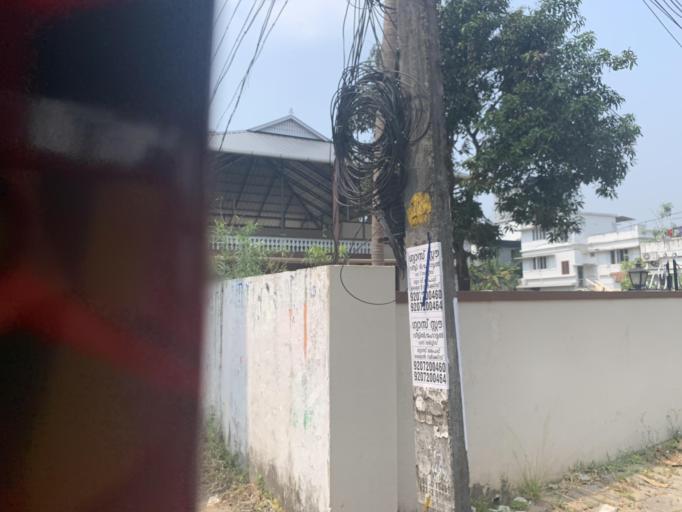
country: IN
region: Kerala
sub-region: Ernakulam
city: Cochin
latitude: 9.9407
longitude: 76.3075
